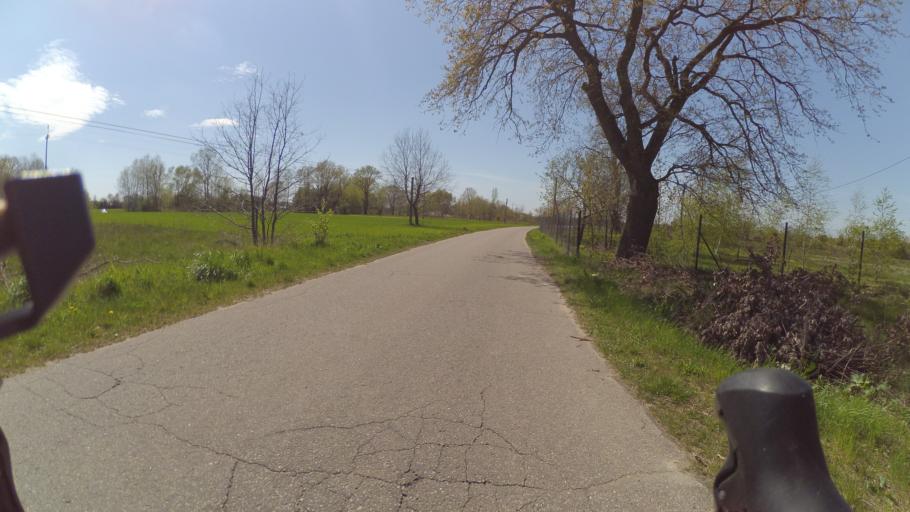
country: PL
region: Masovian Voivodeship
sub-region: Powiat nowodworski
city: Zakroczym
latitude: 52.4167
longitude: 20.5405
